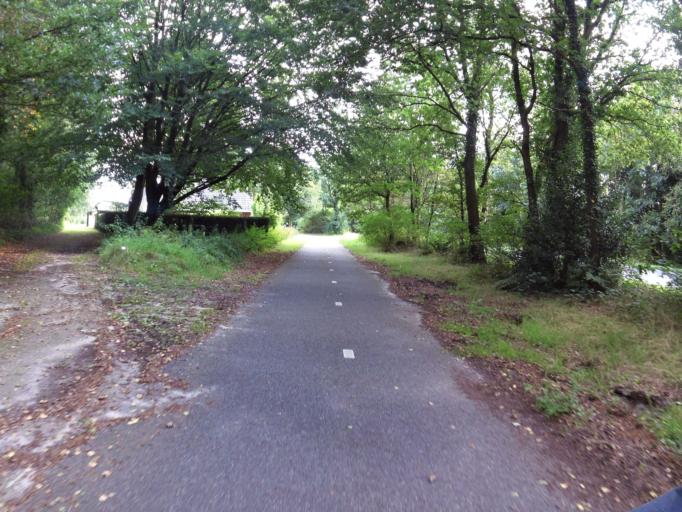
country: NL
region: Drenthe
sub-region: Gemeente Borger-Odoorn
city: Borger
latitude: 52.9334
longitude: 6.7511
